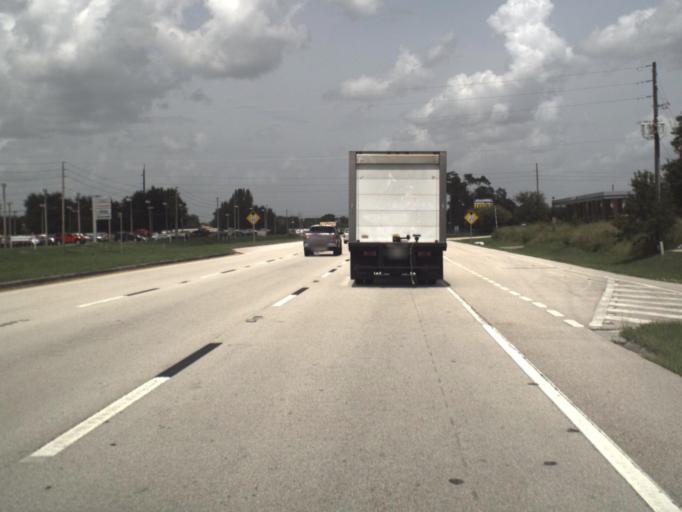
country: US
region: Florida
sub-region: Highlands County
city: Avon Park
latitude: 27.5750
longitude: -81.5143
